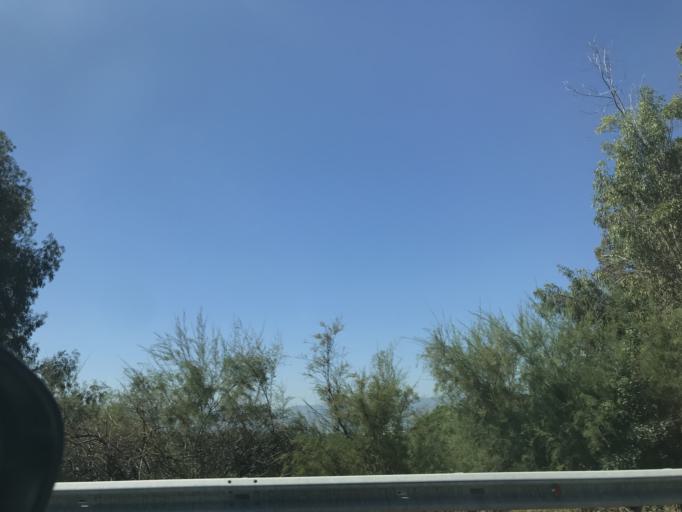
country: TR
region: Aydin
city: Acarlar
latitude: 37.8612
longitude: 27.7840
